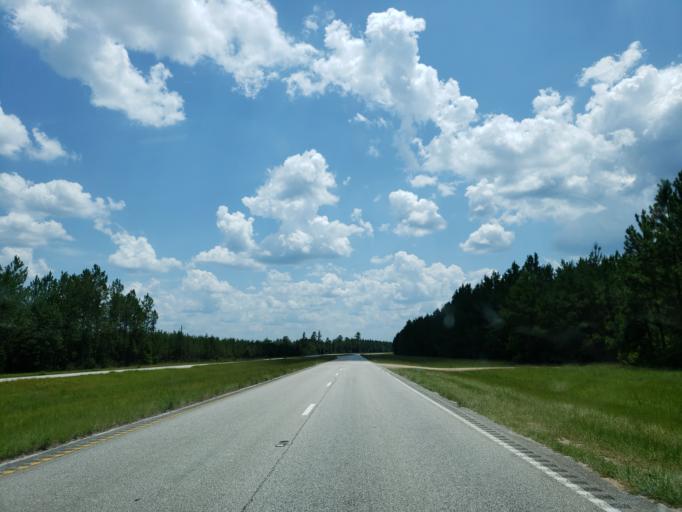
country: US
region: Mississippi
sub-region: Greene County
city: Leakesville
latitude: 31.2986
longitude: -88.5004
